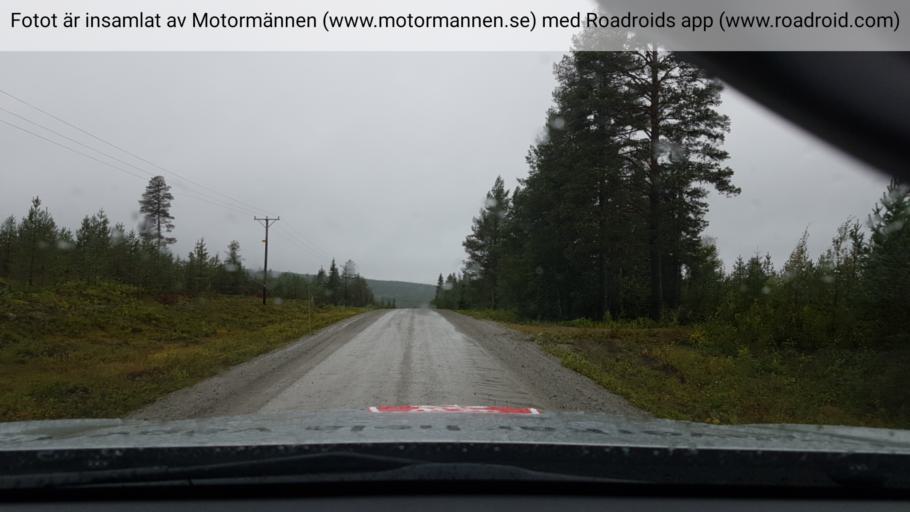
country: SE
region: Vaesterbotten
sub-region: Asele Kommun
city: Insjon
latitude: 64.0859
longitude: 17.8411
